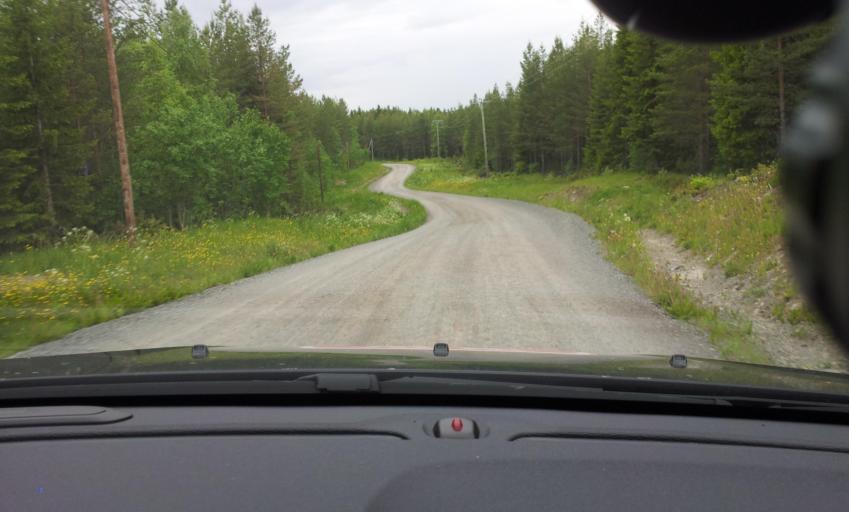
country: SE
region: Jaemtland
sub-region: OEstersunds Kommun
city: Brunflo
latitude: 62.9759
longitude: 14.6589
